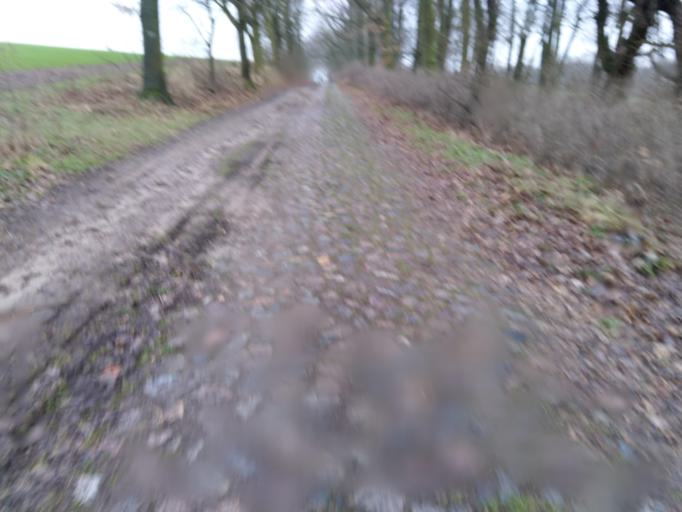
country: DE
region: Brandenburg
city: Ahrensfelde
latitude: 52.6015
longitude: 13.6316
